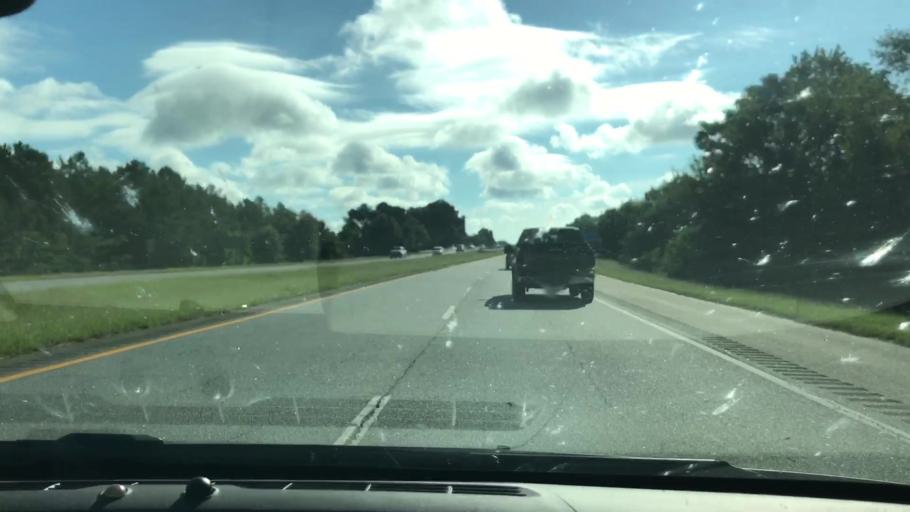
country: US
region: Georgia
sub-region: Dougherty County
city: Albany
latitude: 31.6164
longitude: -84.1857
